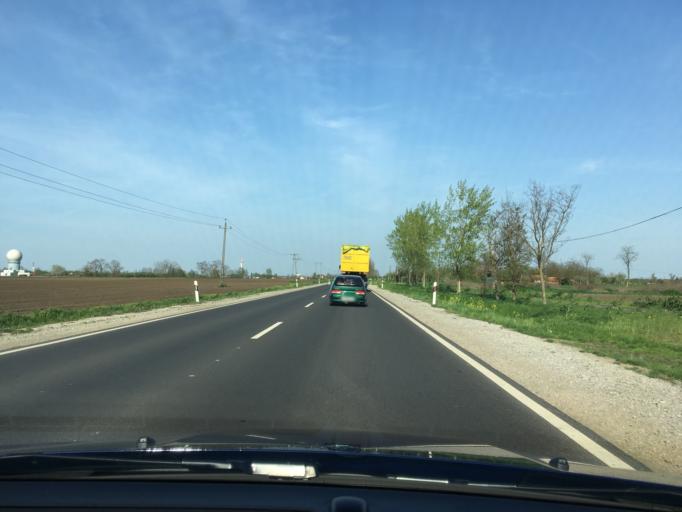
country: HU
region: Bekes
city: Bekescsaba
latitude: 46.6747
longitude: 21.0065
